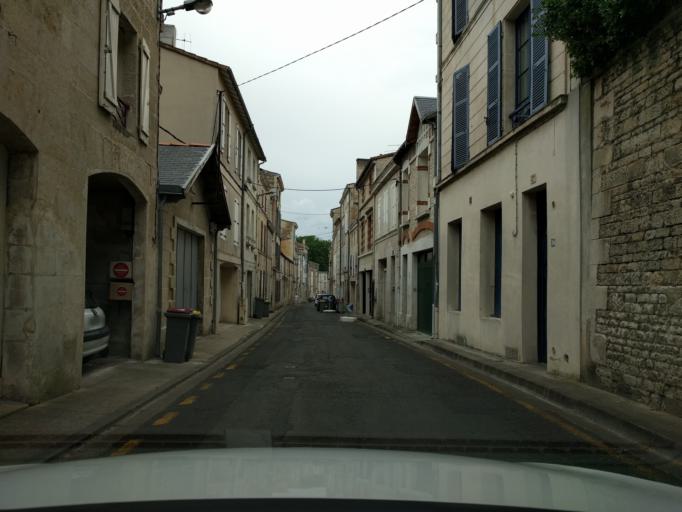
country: FR
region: Poitou-Charentes
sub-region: Departement des Deux-Sevres
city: Niort
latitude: 46.3260
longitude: -0.4586
